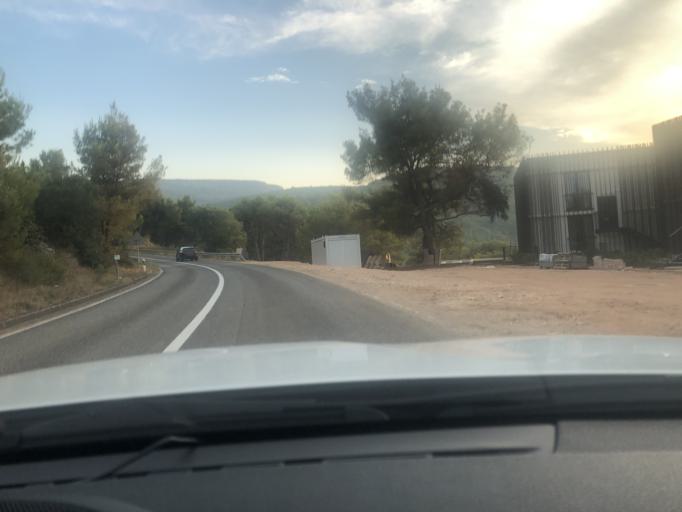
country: HR
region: Splitsko-Dalmatinska
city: Stari Grad
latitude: 43.1799
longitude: 16.5724
